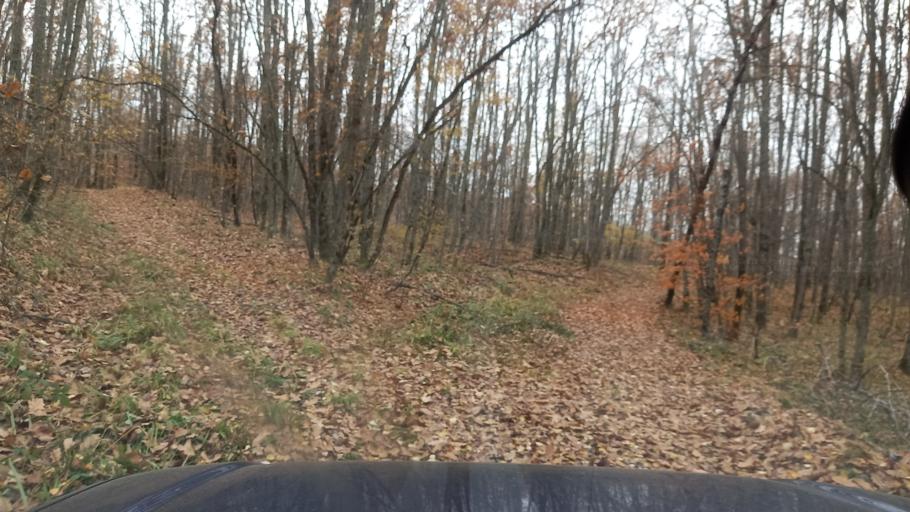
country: RU
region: Krasnodarskiy
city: Goryachiy Klyuch
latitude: 44.4978
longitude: 39.2775
